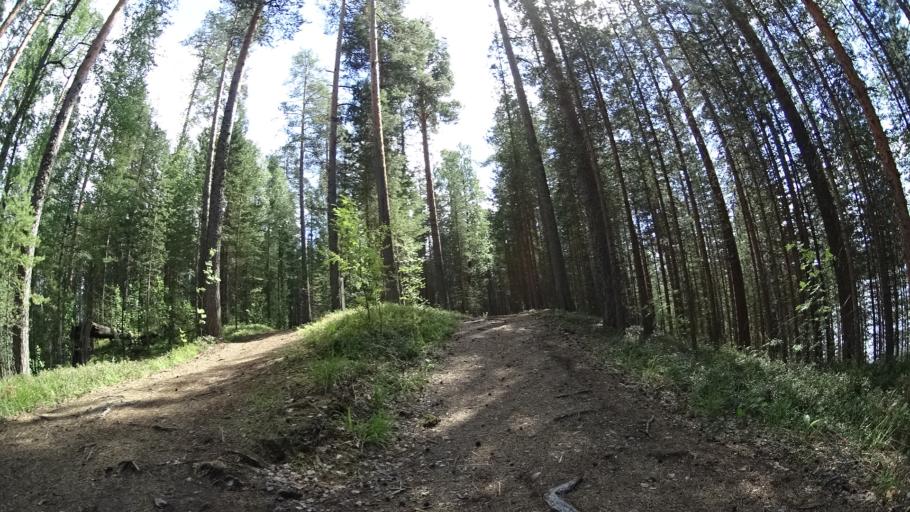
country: FI
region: Southern Savonia
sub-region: Savonlinna
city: Punkaharju
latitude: 61.7908
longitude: 29.3073
